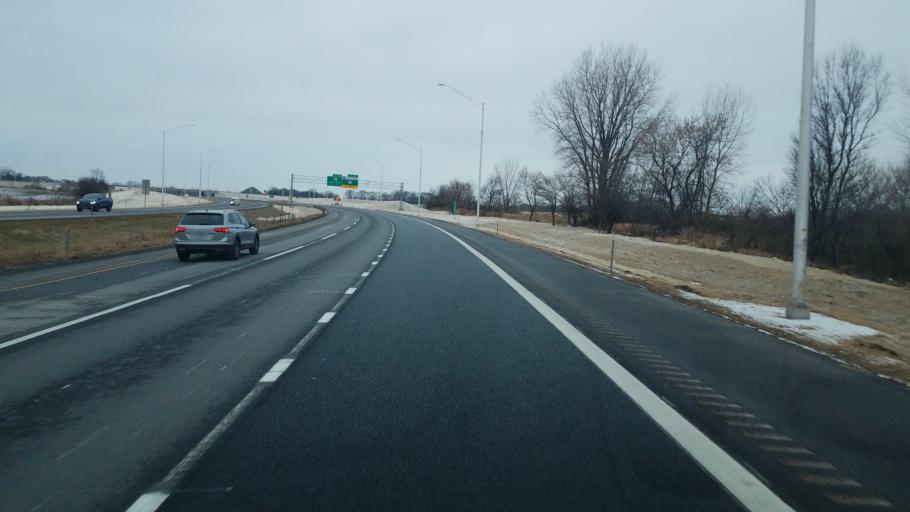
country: US
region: Illinois
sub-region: Kane County
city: Sugar Grove
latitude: 41.8169
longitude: -88.4565
